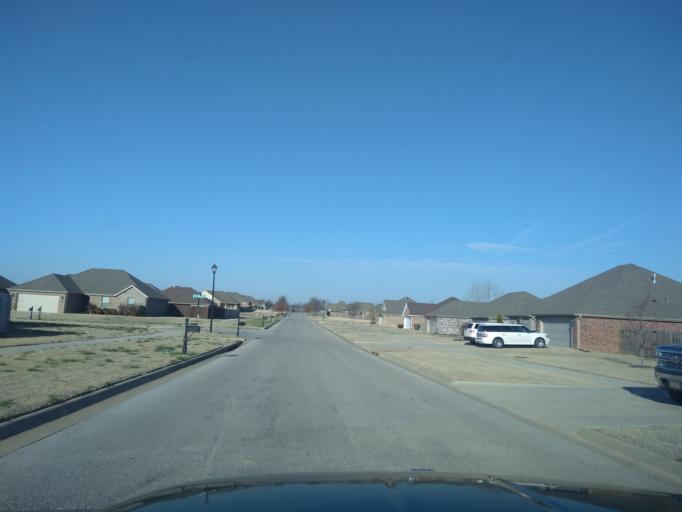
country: US
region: Arkansas
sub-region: Washington County
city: Farmington
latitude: 36.0710
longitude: -94.2456
